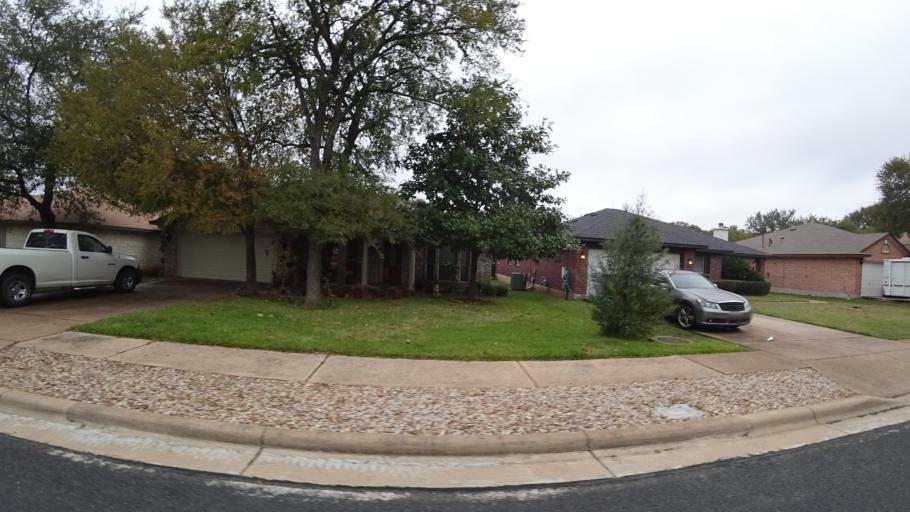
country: US
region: Texas
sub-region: Travis County
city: Shady Hollow
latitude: 30.1872
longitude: -97.8442
